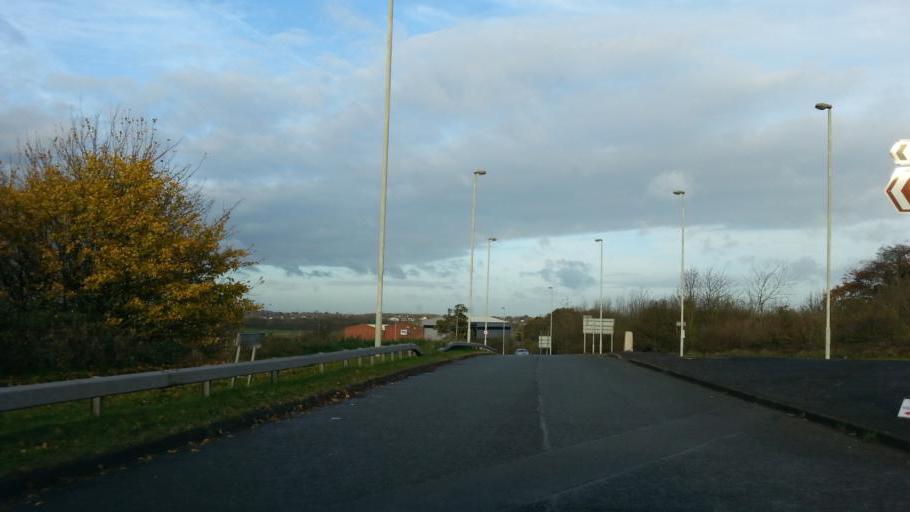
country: GB
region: England
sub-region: Leicestershire
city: Coalville
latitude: 52.7085
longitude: -1.3415
